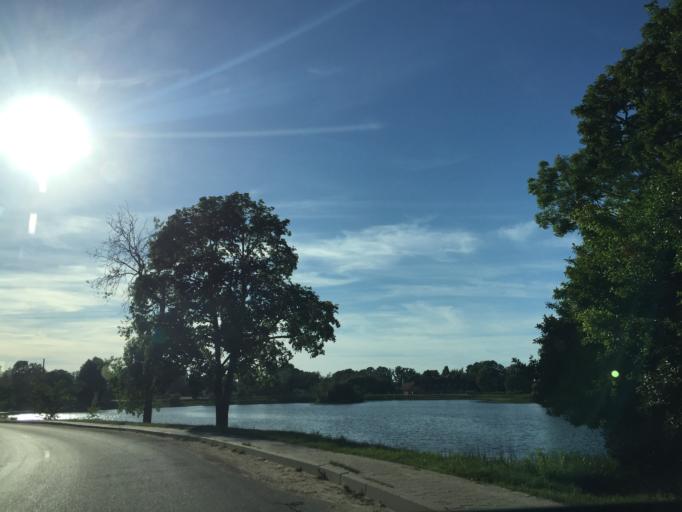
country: LV
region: Alsunga
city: Alsunga
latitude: 57.0179
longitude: 21.6940
